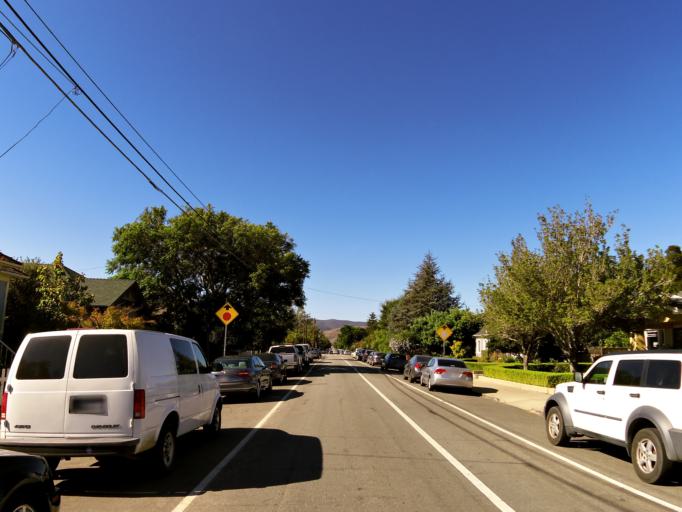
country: US
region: California
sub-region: San Luis Obispo County
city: San Luis Obispo
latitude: 35.2804
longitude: -120.6562
